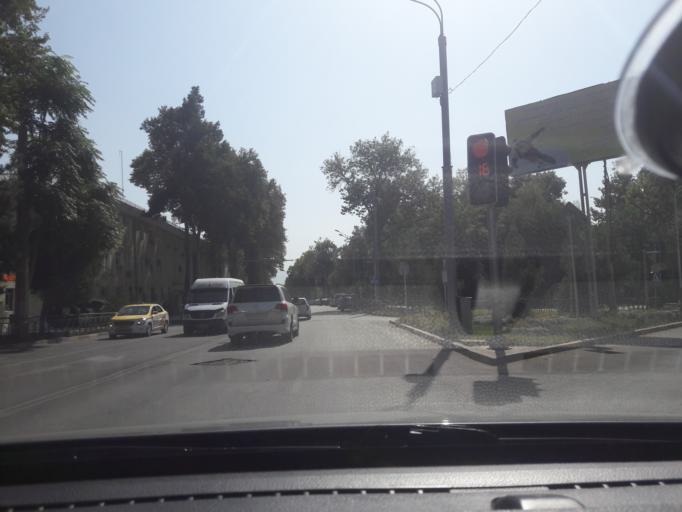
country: TJ
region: Dushanbe
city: Dushanbe
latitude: 38.5723
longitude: 68.8000
